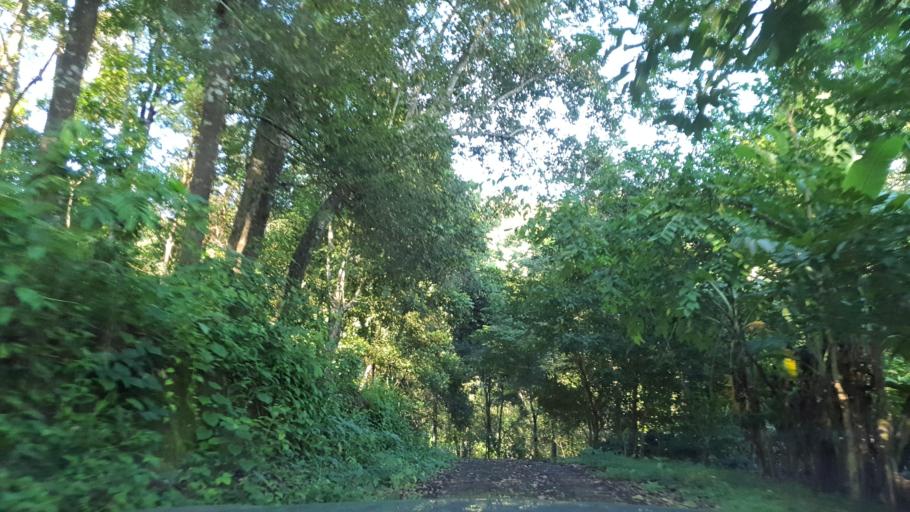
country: TH
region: Chiang Mai
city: Mae On
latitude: 18.8139
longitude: 99.3494
